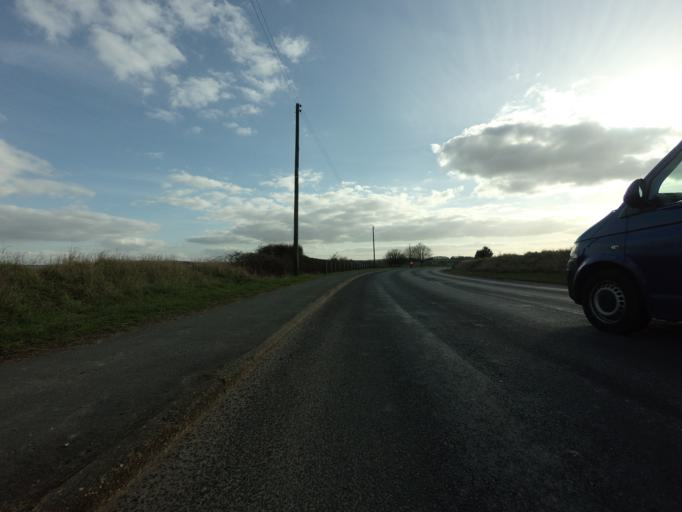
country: GB
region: England
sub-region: Kent
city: Dartford
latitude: 51.4179
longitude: 0.2012
